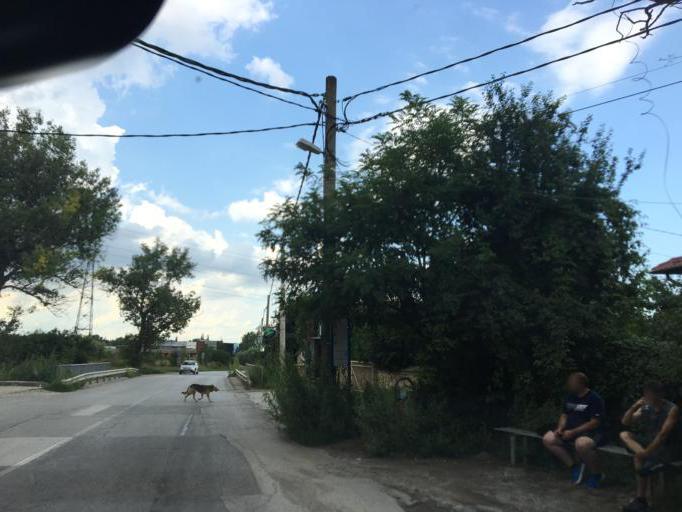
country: BG
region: Sofia-Capital
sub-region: Stolichna Obshtina
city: Sofia
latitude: 42.6265
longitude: 23.3588
